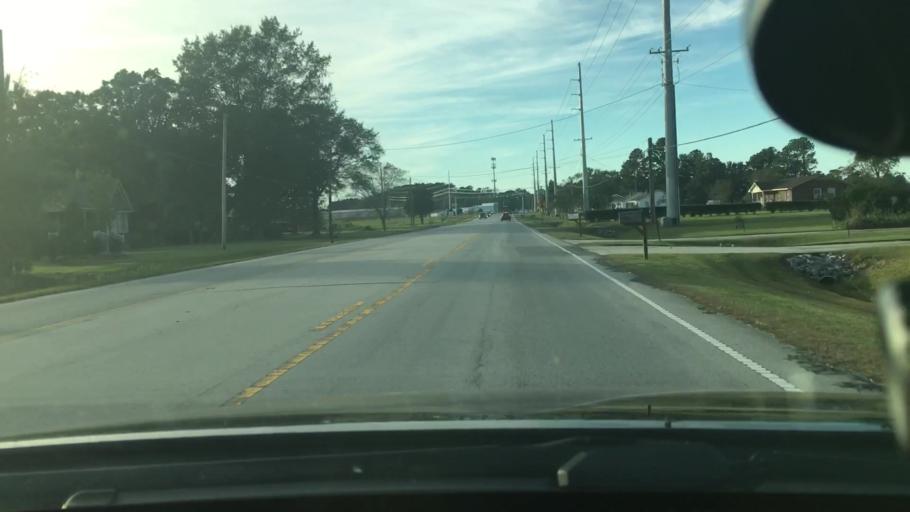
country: US
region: North Carolina
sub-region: Pitt County
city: Windsor
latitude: 35.5615
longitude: -77.3433
